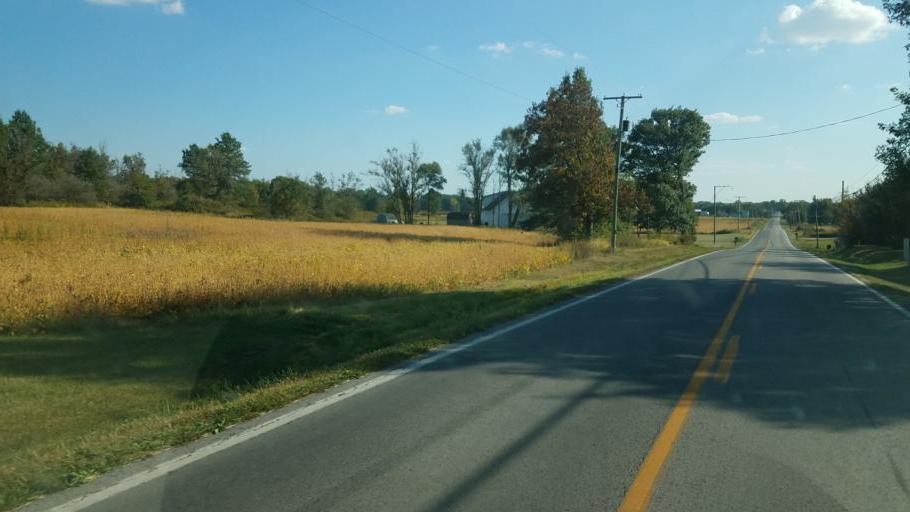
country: US
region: Ohio
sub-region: Union County
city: Richwood
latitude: 40.5981
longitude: -83.3804
